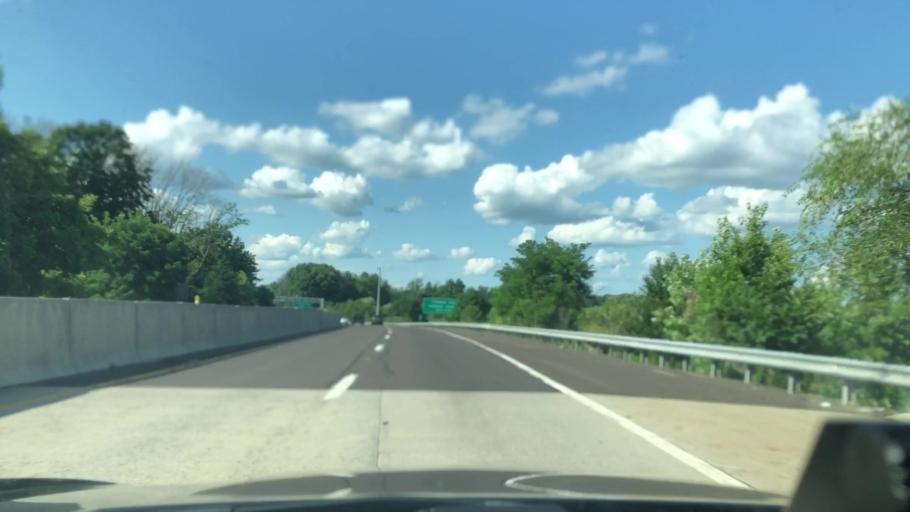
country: US
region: Pennsylvania
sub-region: Montgomery County
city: Fort Washington
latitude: 40.1537
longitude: -75.2017
